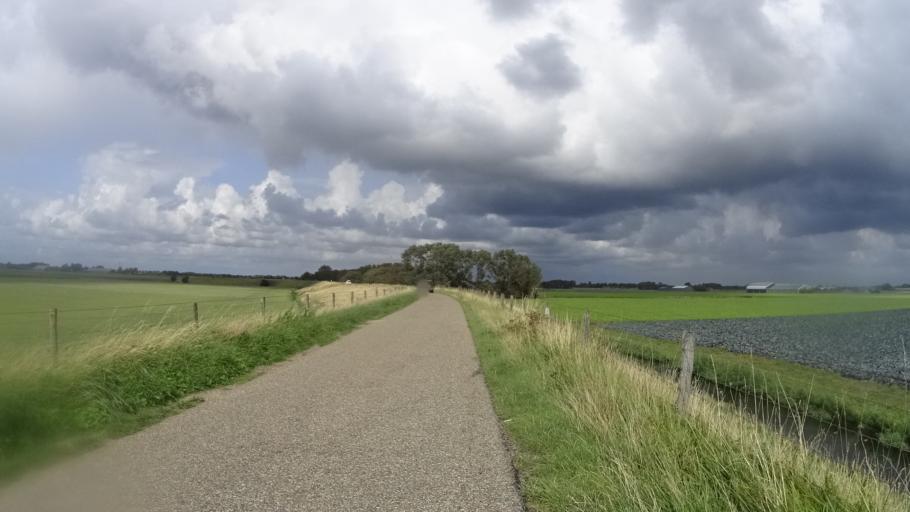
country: NL
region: North Holland
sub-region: Gemeente Schagen
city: Harenkarspel
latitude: 52.7579
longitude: 4.7263
